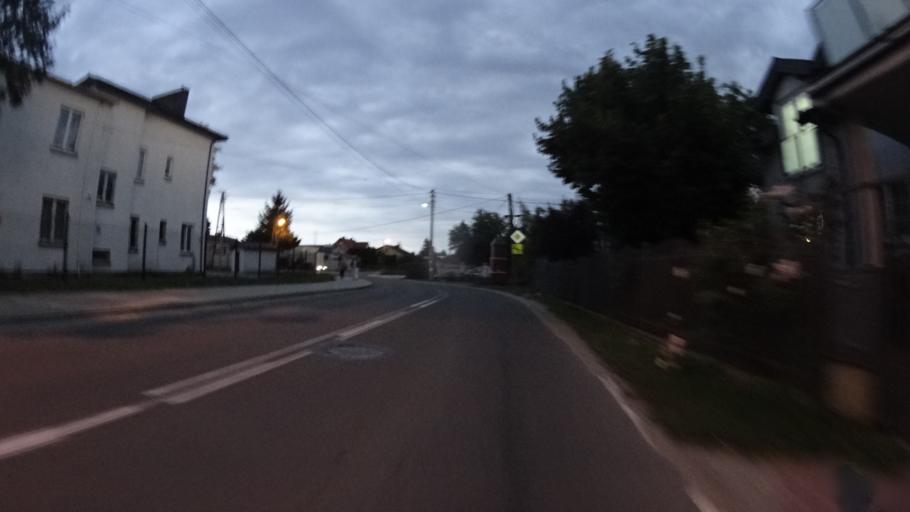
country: PL
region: Masovian Voivodeship
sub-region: Powiat warszawski zachodni
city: Babice
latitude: 52.2238
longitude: 20.8599
